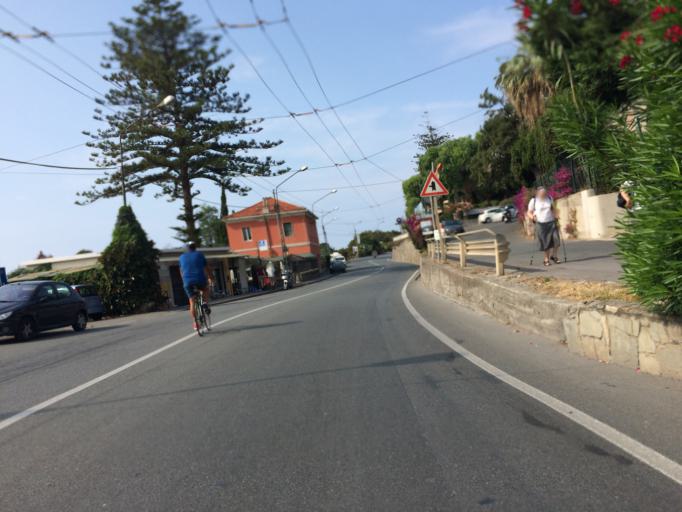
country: IT
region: Liguria
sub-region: Provincia di Imperia
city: Ospedaletti
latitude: 43.8042
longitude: 7.7467
